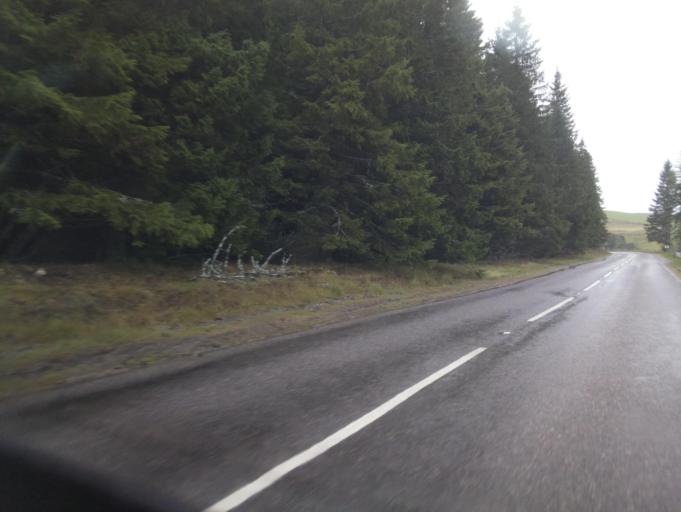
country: GB
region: Scotland
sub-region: Aberdeenshire
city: Ballater
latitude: 57.1626
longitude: -3.2206
